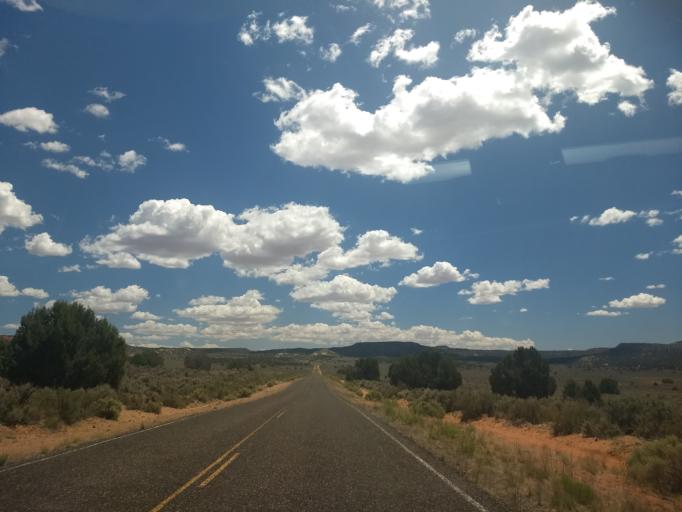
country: US
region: Utah
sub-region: Kane County
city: Kanab
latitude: 37.1692
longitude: -112.6629
